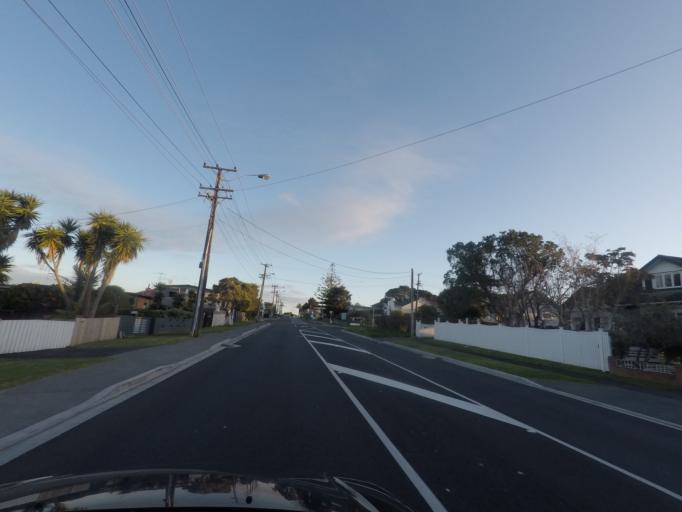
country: NZ
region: Auckland
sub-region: Auckland
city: Rosebank
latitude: -36.8820
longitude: 174.6460
